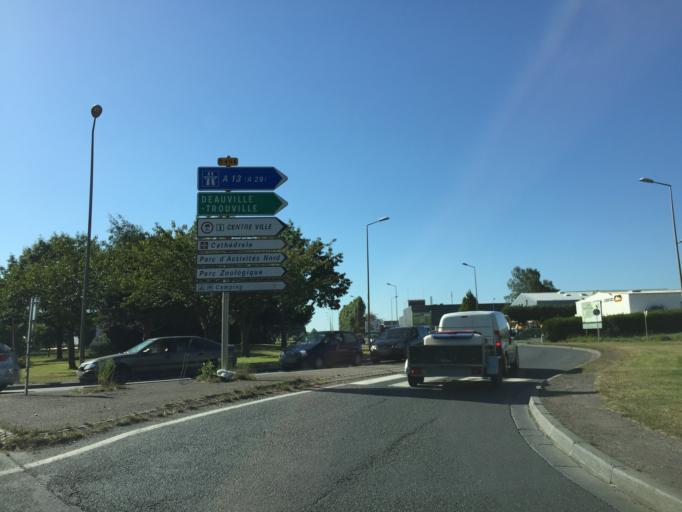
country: FR
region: Lower Normandy
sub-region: Departement du Calvados
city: Beuvillers
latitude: 49.1450
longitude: 0.2631
